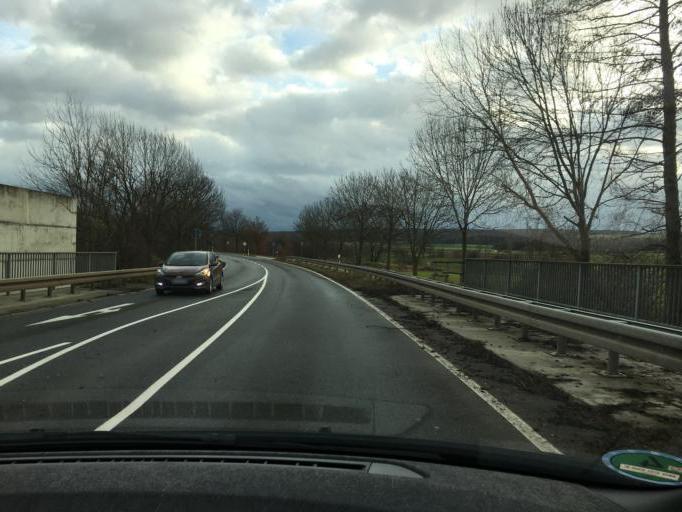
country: DE
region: North Rhine-Westphalia
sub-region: Regierungsbezirk Koln
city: Euskirchen
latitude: 50.6518
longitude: 6.7461
